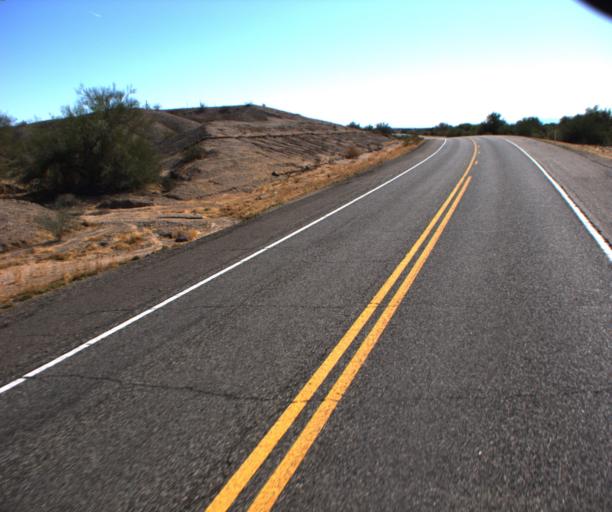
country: US
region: Arizona
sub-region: La Paz County
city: Parker
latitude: 33.9930
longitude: -114.2076
